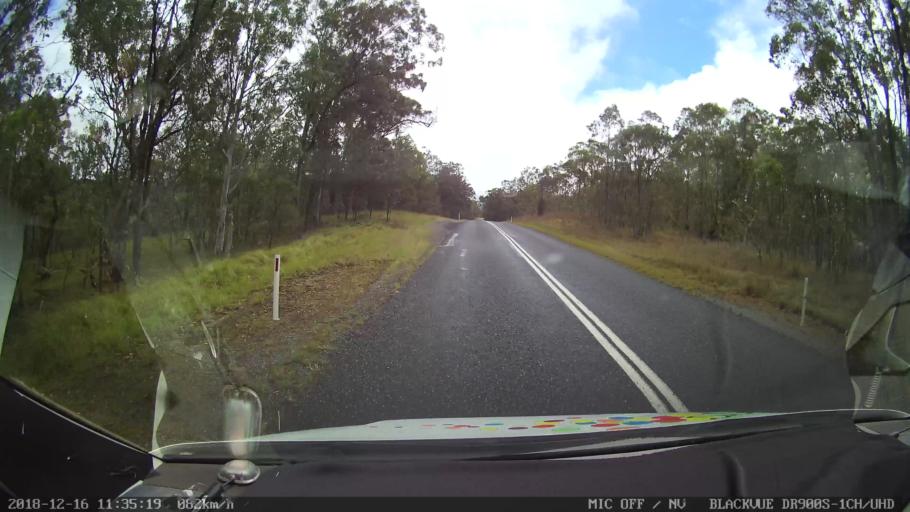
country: AU
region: New South Wales
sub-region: Tenterfield Municipality
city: Carrolls Creek
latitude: -28.9911
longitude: 152.1616
